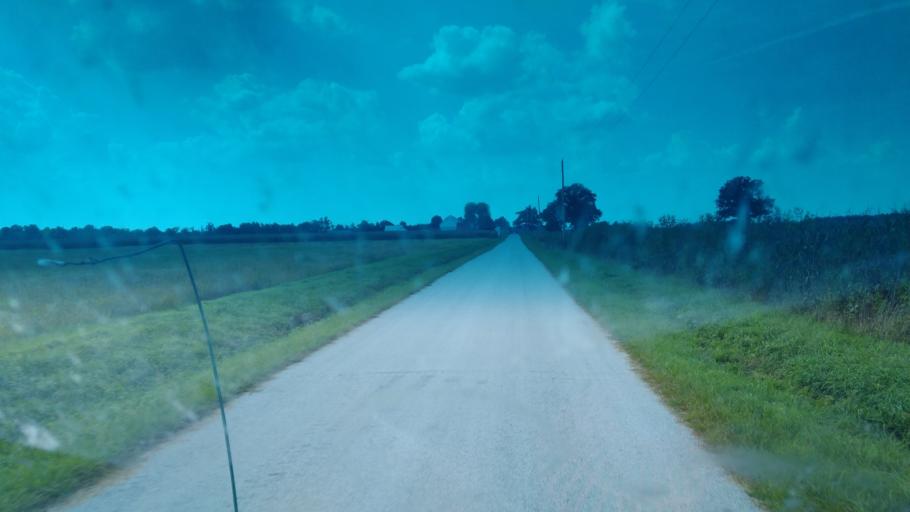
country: US
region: Ohio
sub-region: Hardin County
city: Kenton
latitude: 40.6893
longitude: -83.7152
